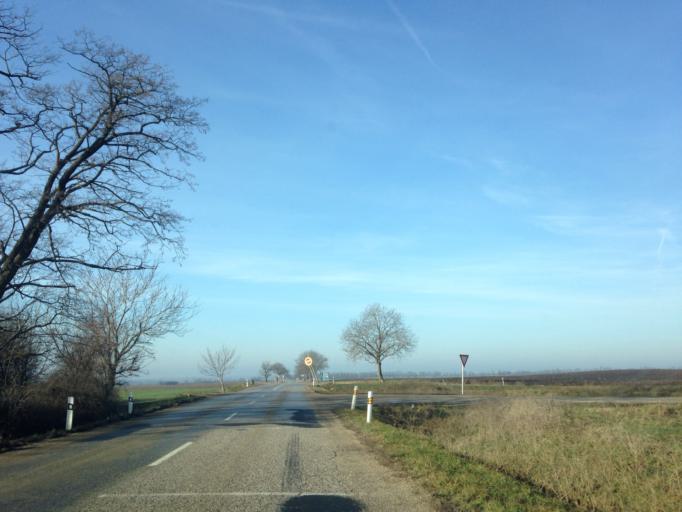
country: SK
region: Nitriansky
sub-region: Okres Nove Zamky
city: Nove Zamky
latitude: 47.9897
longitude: 18.3307
